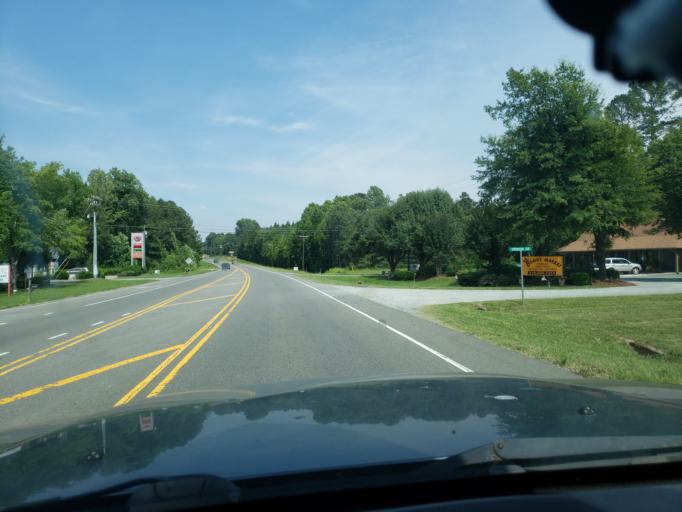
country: US
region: North Carolina
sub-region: Orange County
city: Carrboro
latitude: 35.9220
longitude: -79.1862
